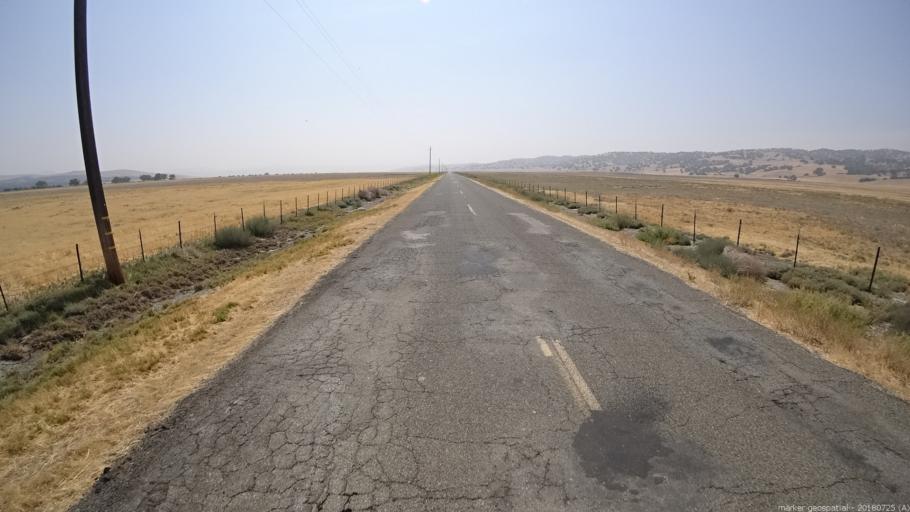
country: US
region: California
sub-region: San Luis Obispo County
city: Shandon
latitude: 35.8024
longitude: -120.3531
